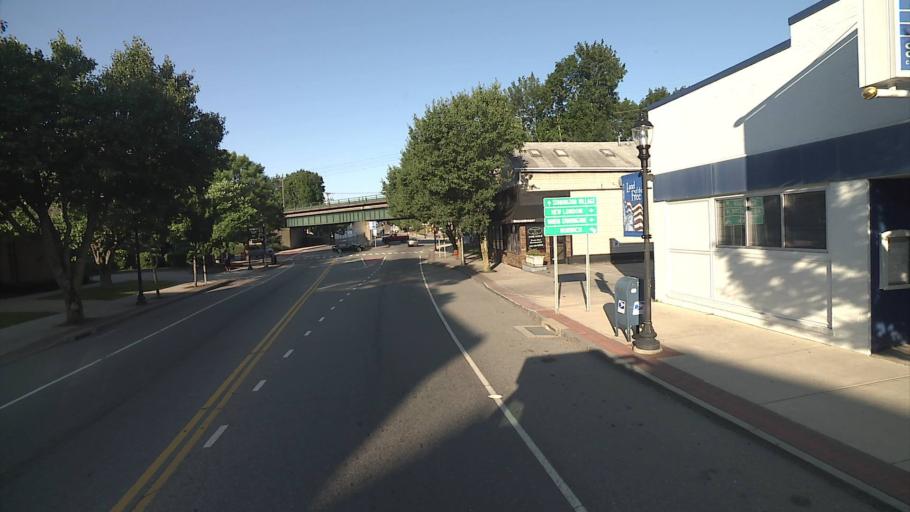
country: US
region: Connecticut
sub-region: New London County
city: Pawcatuck
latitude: 41.3776
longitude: -71.8326
